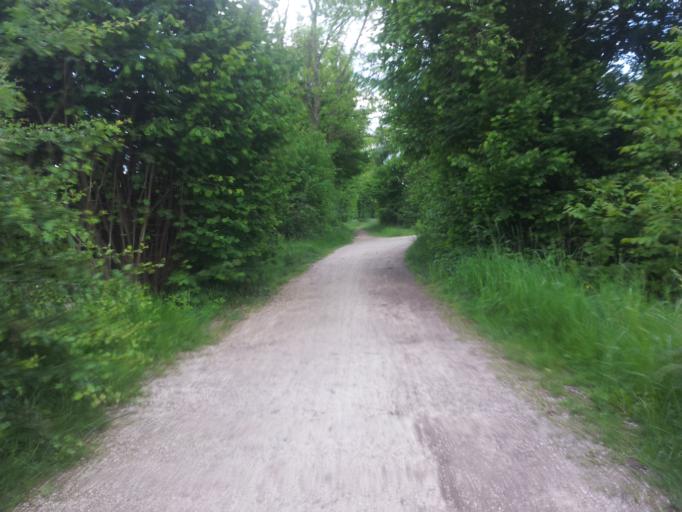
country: DE
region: Baden-Wuerttemberg
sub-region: Regierungsbezirk Stuttgart
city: Wernau
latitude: 48.6995
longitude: 9.4167
